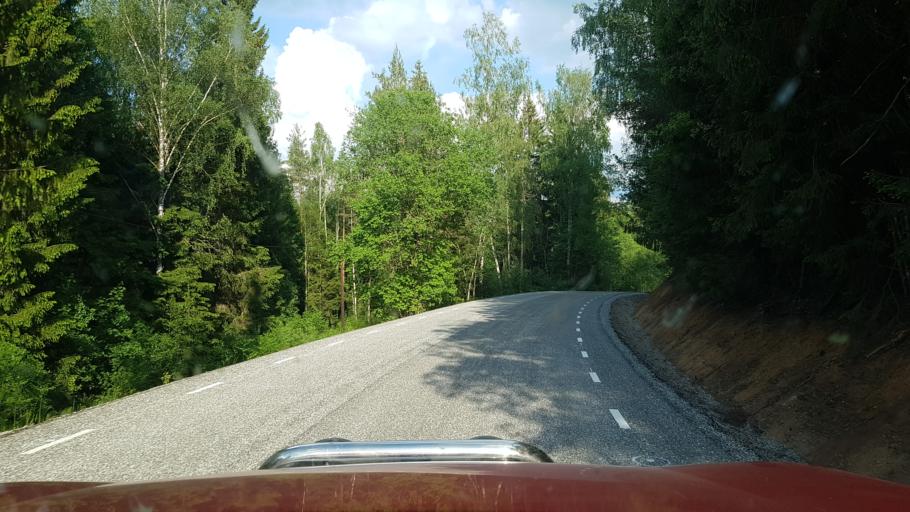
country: EE
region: Tartu
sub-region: UElenurme vald
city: Ulenurme
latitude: 58.1075
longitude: 26.7545
